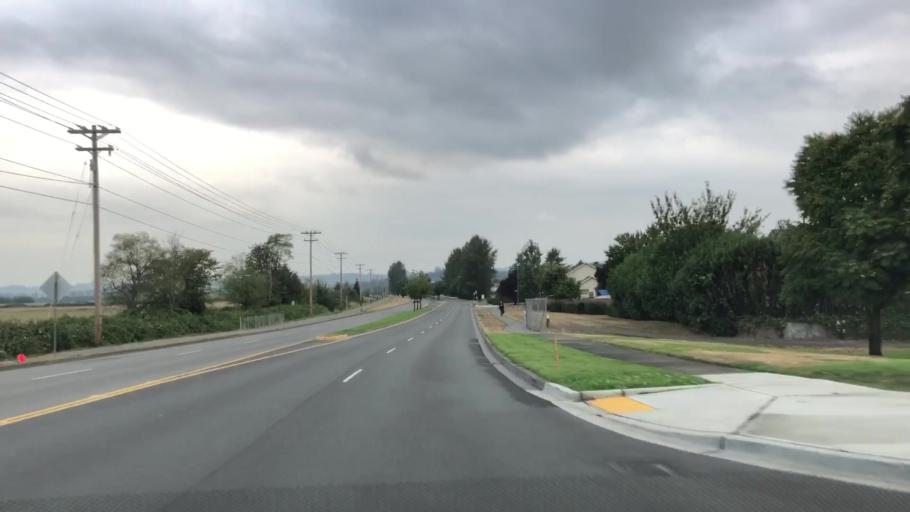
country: US
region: Washington
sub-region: Snohomish County
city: Monroe
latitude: 47.8502
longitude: -122.0120
